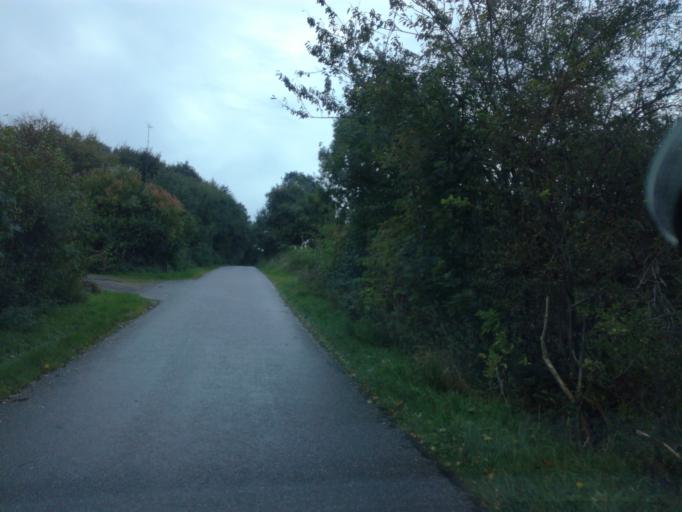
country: DK
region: South Denmark
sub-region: Fredericia Kommune
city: Fredericia
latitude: 55.6029
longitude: 9.7165
